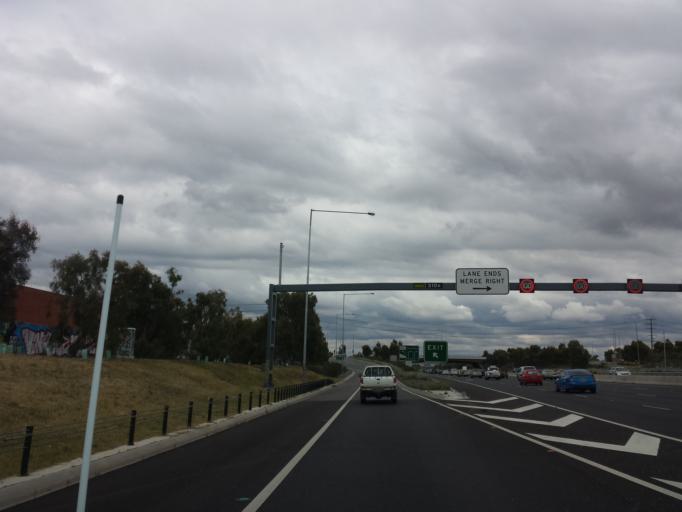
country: AU
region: Victoria
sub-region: Whittlesea
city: Thomastown
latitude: -37.6867
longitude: 145.0064
